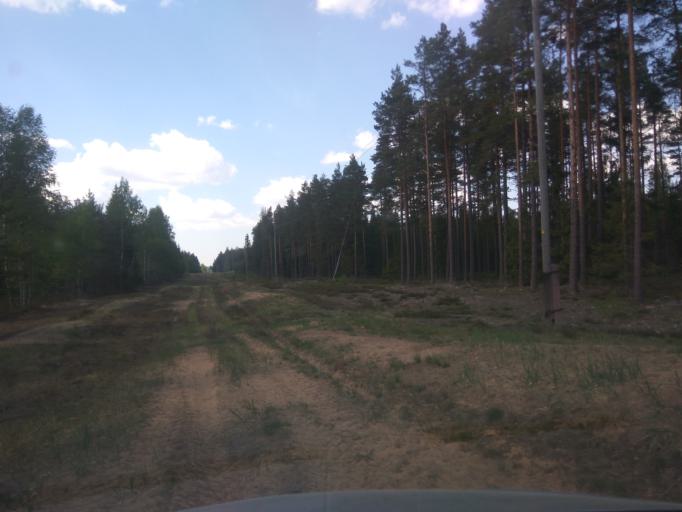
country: LV
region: Kuldigas Rajons
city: Kuldiga
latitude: 57.1828
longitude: 21.9983
